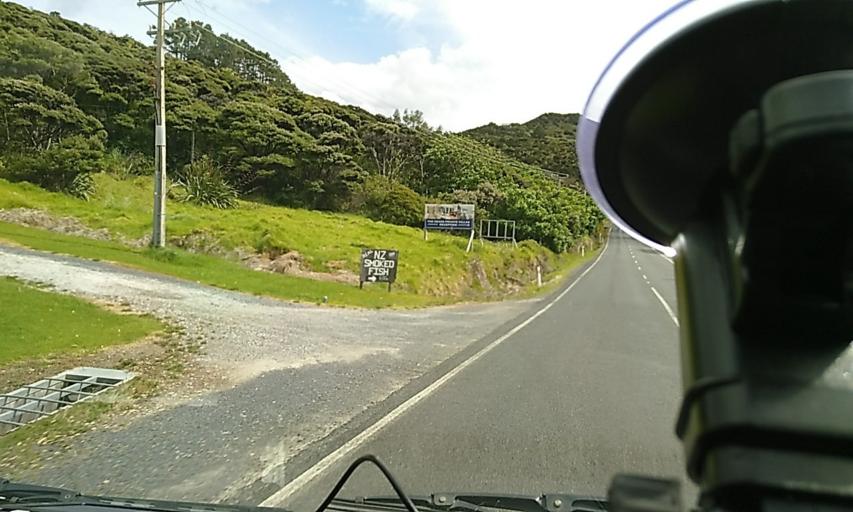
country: NZ
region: Northland
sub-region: Far North District
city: Ahipara
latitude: -35.5352
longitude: 173.3876
